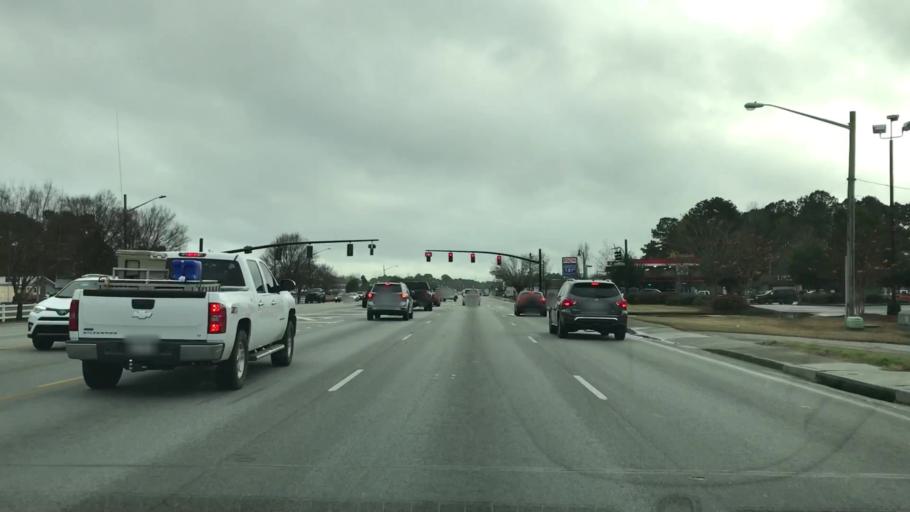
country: US
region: South Carolina
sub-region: Berkeley County
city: Goose Creek
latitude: 33.0021
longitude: -80.0381
